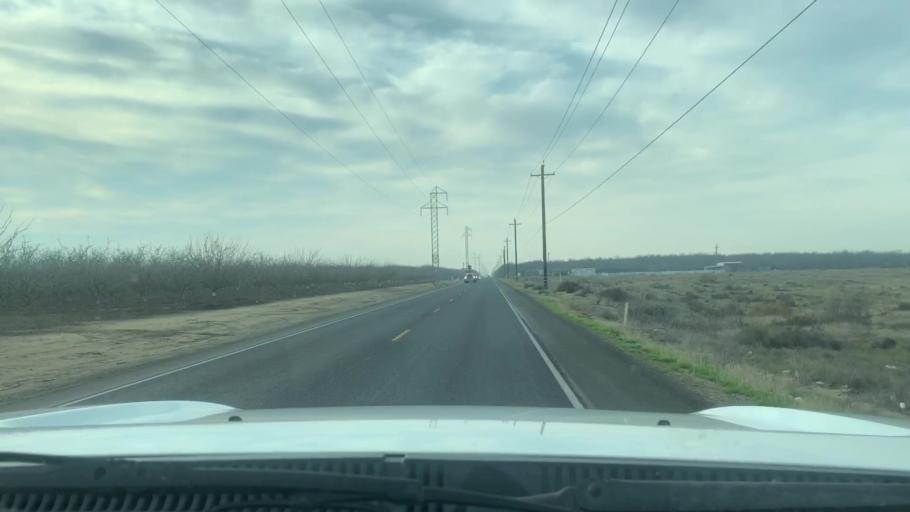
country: US
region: California
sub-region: Kern County
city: Shafter
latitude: 35.4418
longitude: -119.2931
